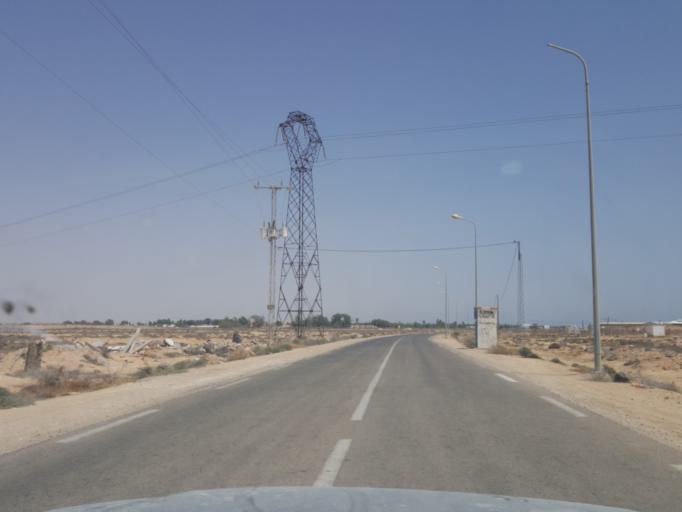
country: TN
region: Qabis
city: Gabes
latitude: 33.9758
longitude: 10.0025
